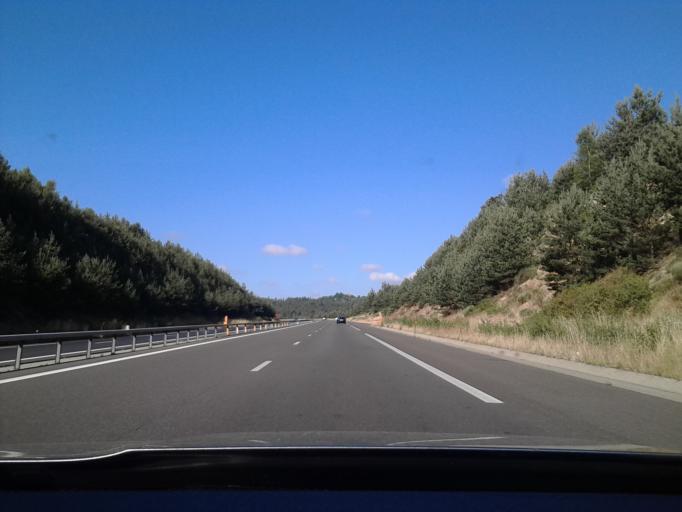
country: FR
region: Languedoc-Roussillon
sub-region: Departement de la Lozere
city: Aumont-Aubrac
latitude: 44.6858
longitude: 3.2688
